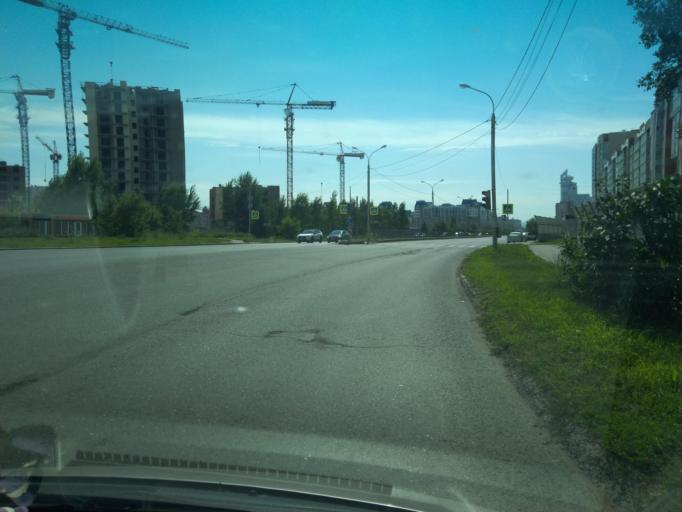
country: RU
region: Krasnoyarskiy
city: Krasnoyarsk
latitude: 56.0501
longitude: 92.9219
